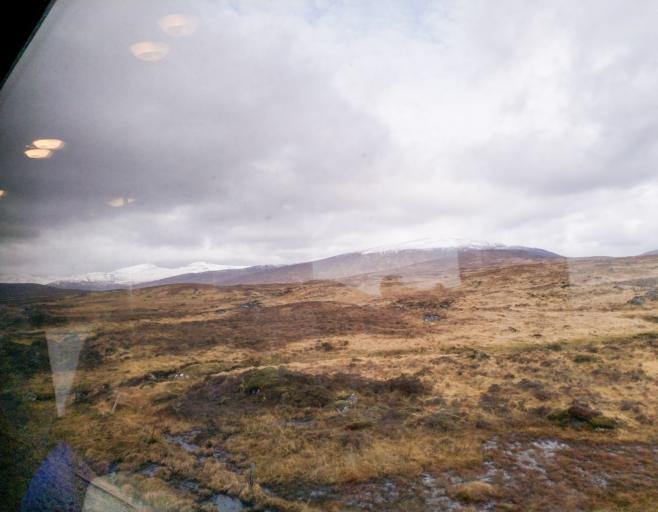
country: GB
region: Scotland
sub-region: Highland
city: Spean Bridge
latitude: 56.7299
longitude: -4.6470
